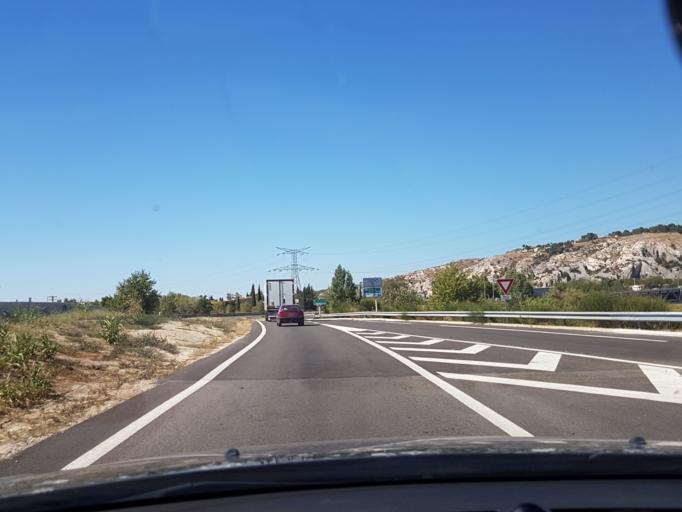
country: FR
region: Provence-Alpes-Cote d'Azur
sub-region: Departement du Vaucluse
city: Cavaillon
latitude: 43.8237
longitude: 5.0292
